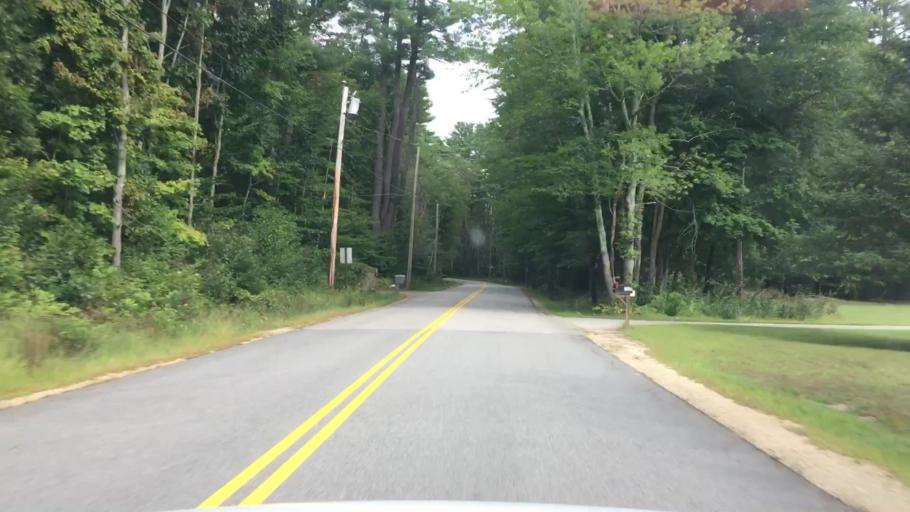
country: US
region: New Hampshire
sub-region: Strafford County
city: Madbury
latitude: 43.2013
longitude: -70.9825
